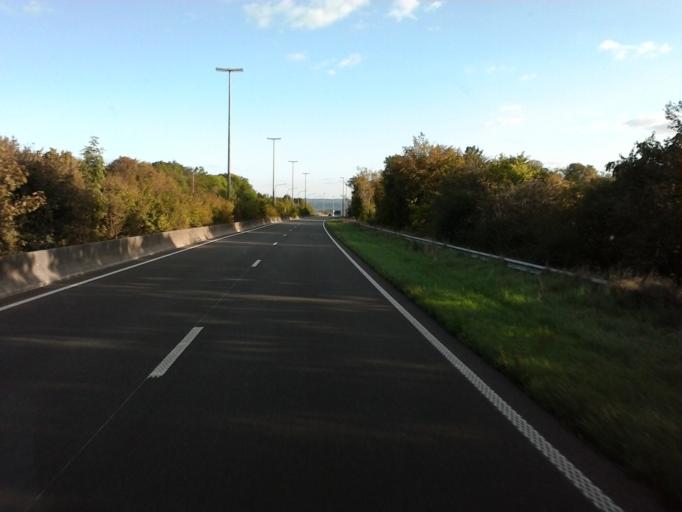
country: BE
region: Wallonia
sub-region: Province de Namur
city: Somme-Leuze
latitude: 50.3031
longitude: 5.3476
